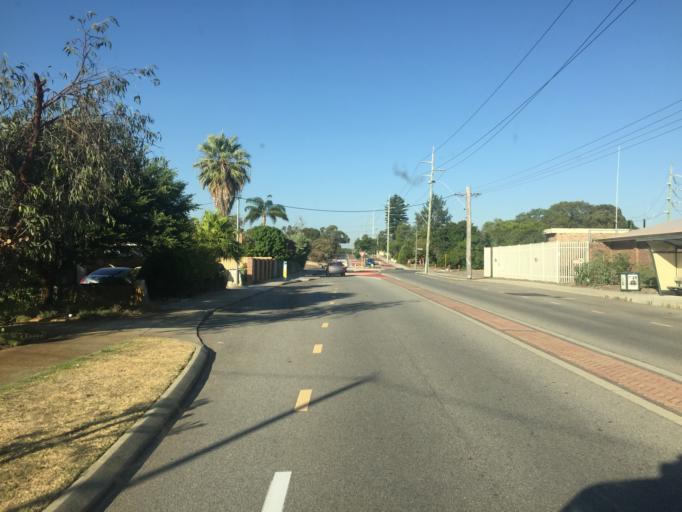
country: AU
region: Western Australia
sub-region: Belmont
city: Belmont
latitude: -31.9554
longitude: 115.9349
